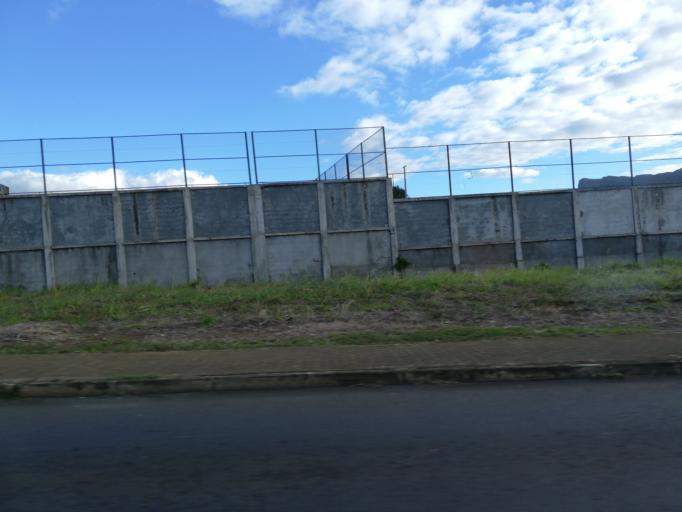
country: MU
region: Plaines Wilhems
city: Ebene
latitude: -20.2393
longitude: 57.4824
